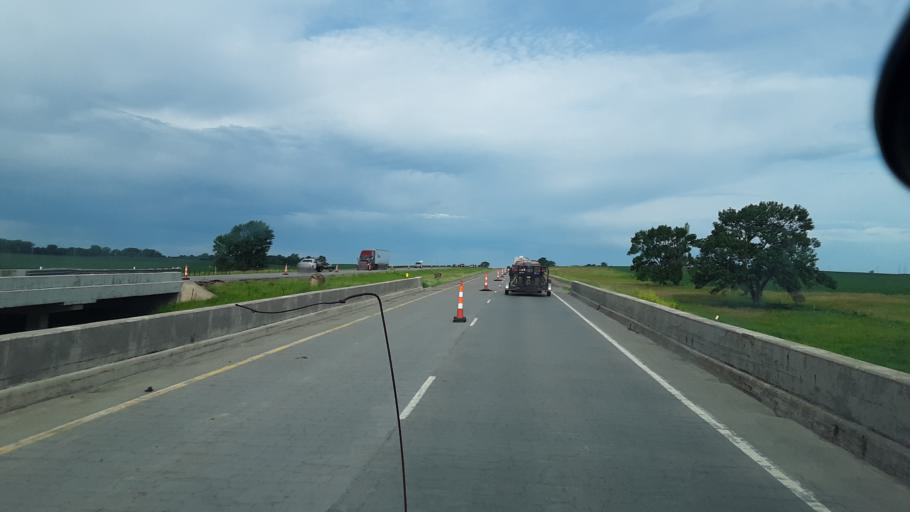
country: US
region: South Dakota
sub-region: Minnehaha County
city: Crooks
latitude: 43.6087
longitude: -96.8503
